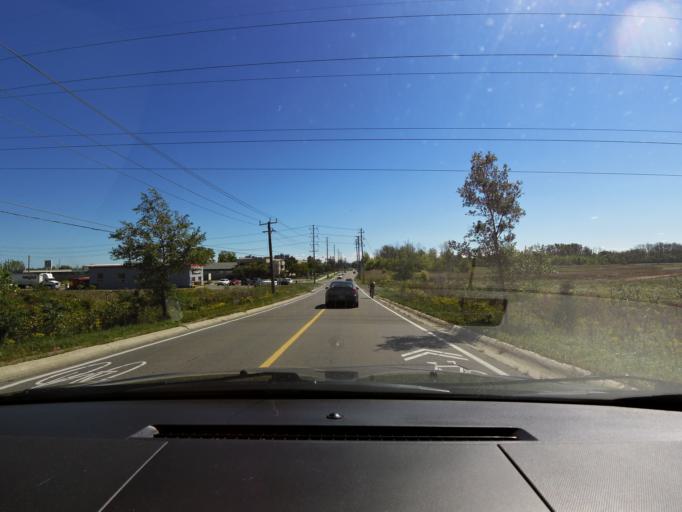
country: CA
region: Ontario
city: Burlington
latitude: 43.3281
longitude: -79.8415
